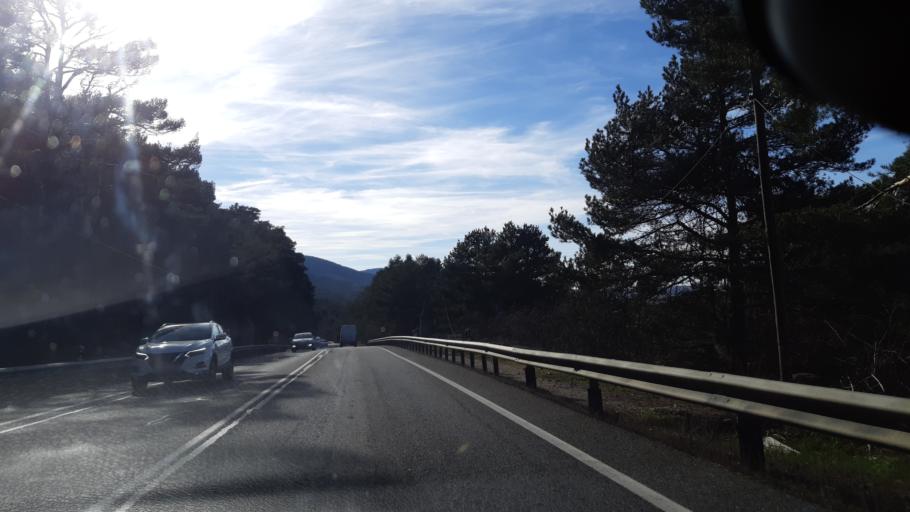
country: ES
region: Madrid
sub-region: Provincia de Madrid
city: Guadarrama
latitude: 40.7122
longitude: -4.1636
